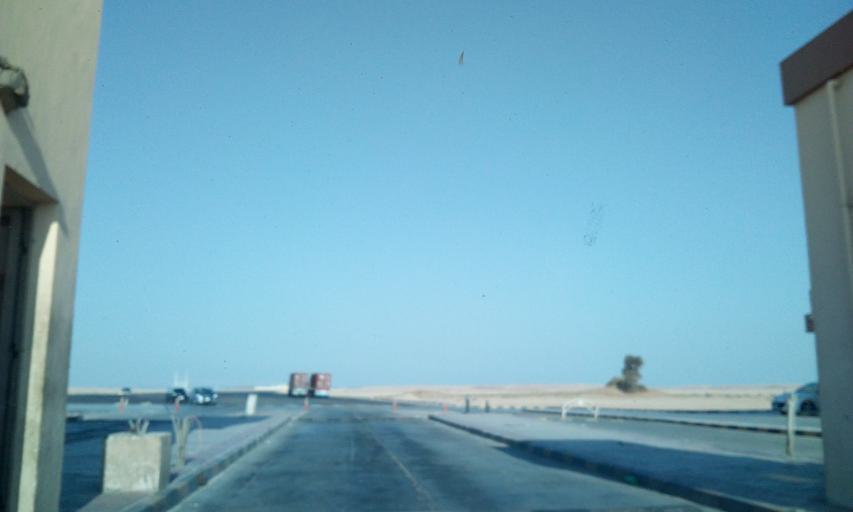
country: EG
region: As Suways
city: Ain Sukhna
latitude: 29.1102
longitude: 32.5496
